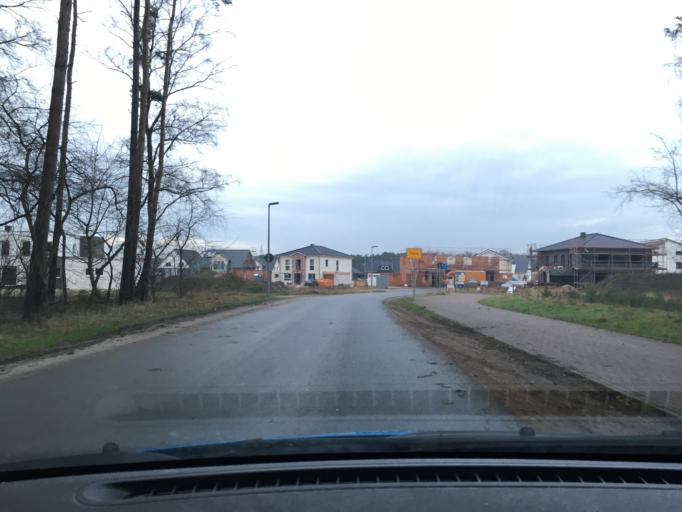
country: DE
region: Lower Saxony
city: Celle
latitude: 52.6393
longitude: 10.0439
